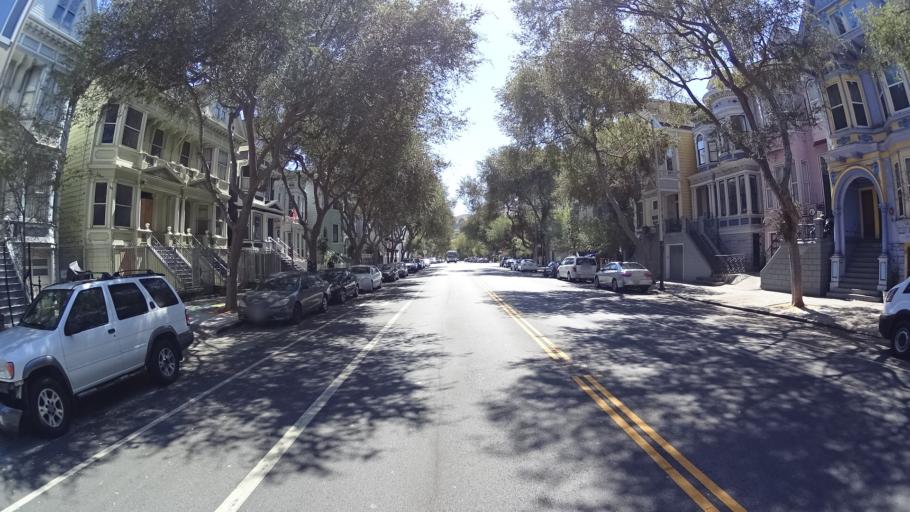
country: US
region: California
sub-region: San Francisco County
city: San Francisco
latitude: 37.7517
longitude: -122.4140
